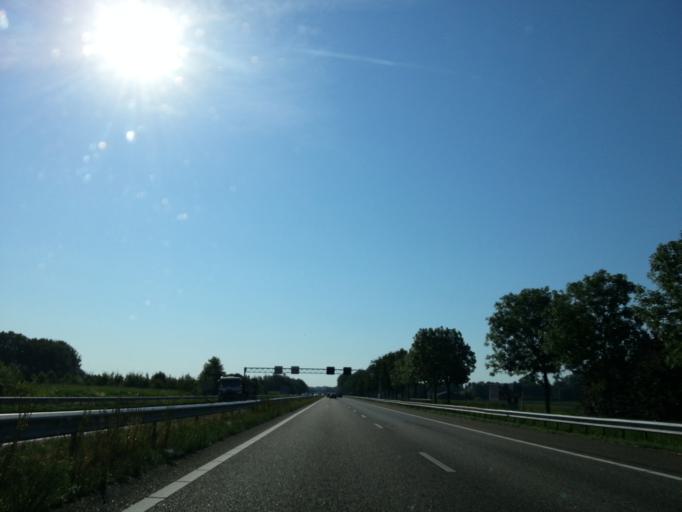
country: NL
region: North Brabant
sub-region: Gemeente Heeze-Leende
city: Heeze
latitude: 51.3422
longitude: 5.5576
